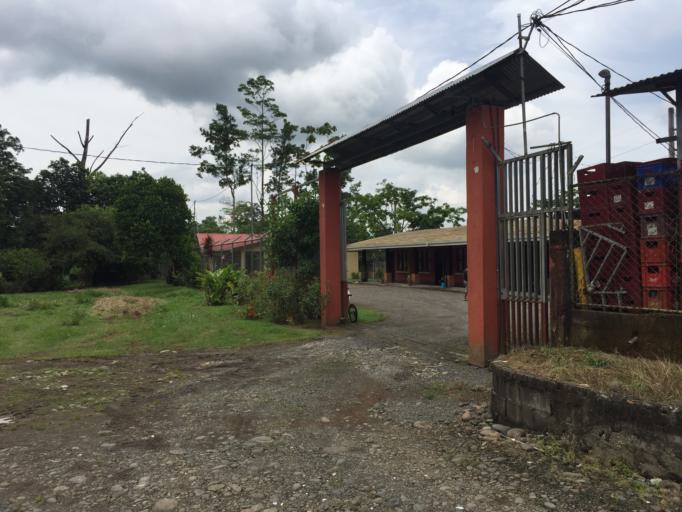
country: CR
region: Heredia
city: La Virgen
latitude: 10.4492
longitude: -84.0129
